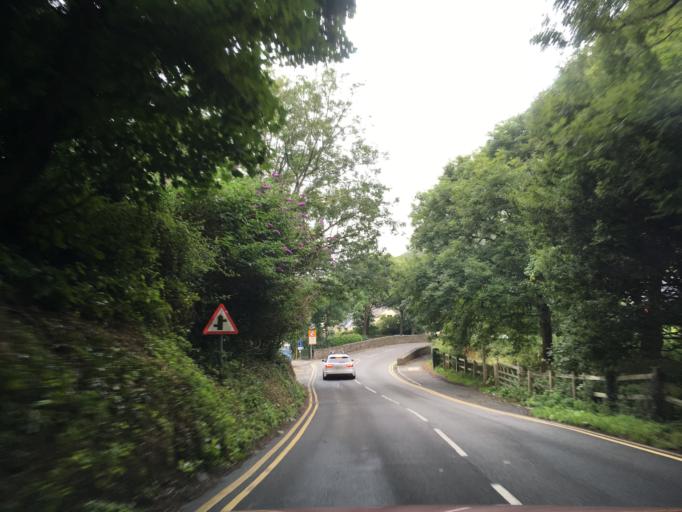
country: GB
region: Wales
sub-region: Pembrokeshire
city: Llanrhian
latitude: 51.8761
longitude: -5.1865
